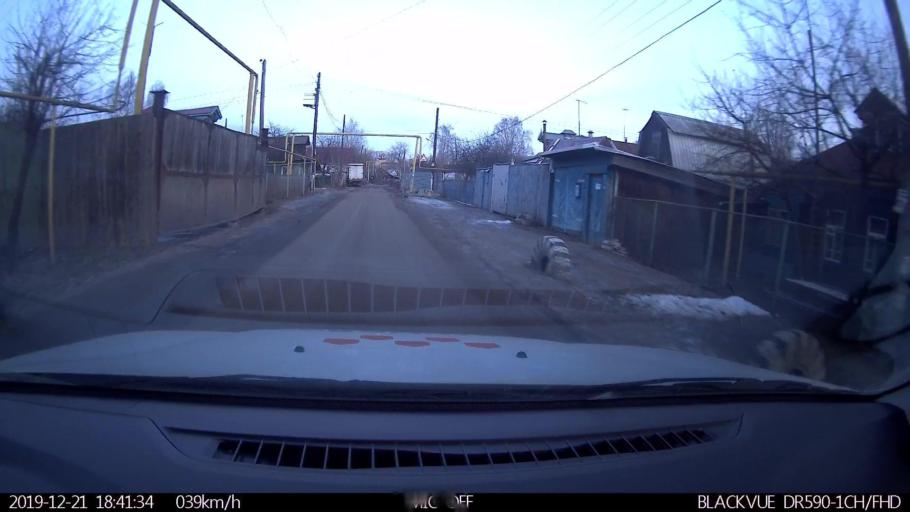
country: RU
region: Nizjnij Novgorod
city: Nizhniy Novgorod
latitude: 56.3286
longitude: 43.9253
